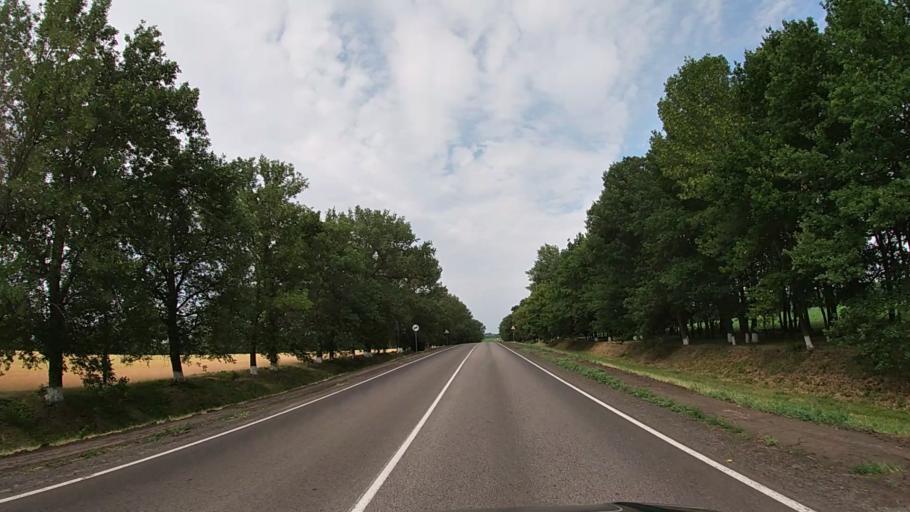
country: RU
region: Belgorod
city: Krasnaya Yaruga
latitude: 50.8104
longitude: 35.5078
